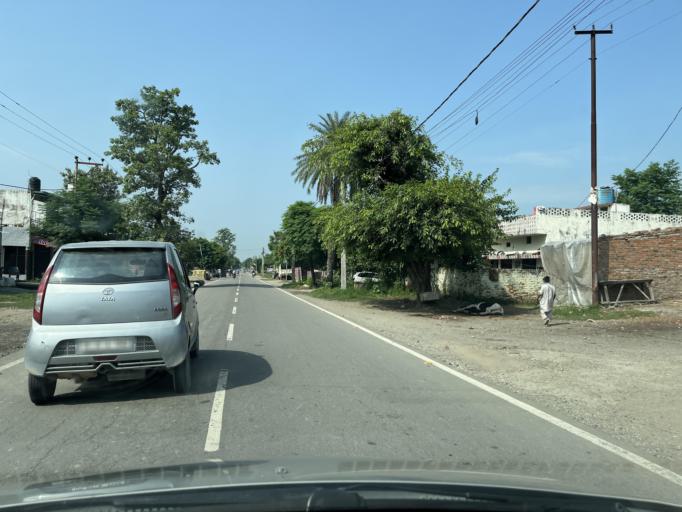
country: IN
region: Uttarakhand
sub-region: Udham Singh Nagar
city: Bazpur
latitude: 29.2072
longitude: 79.2118
